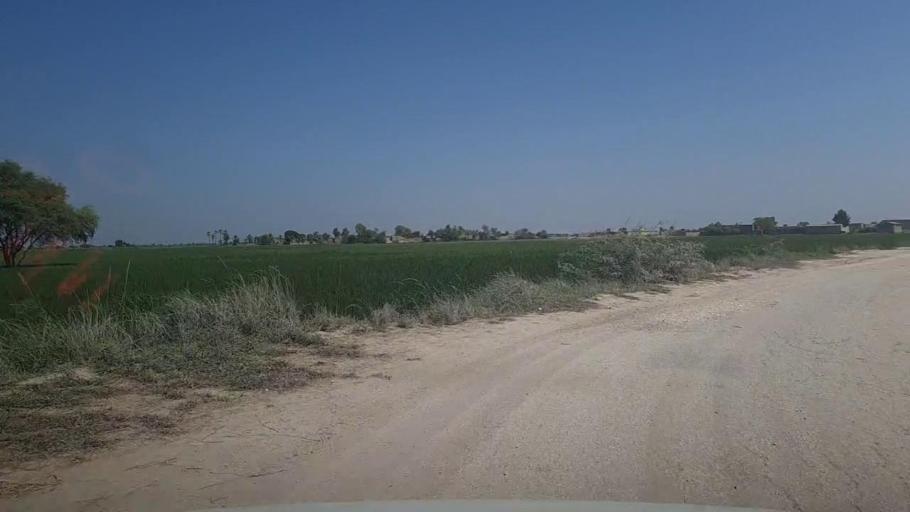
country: PK
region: Sindh
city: Kashmor
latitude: 28.2919
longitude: 69.4343
